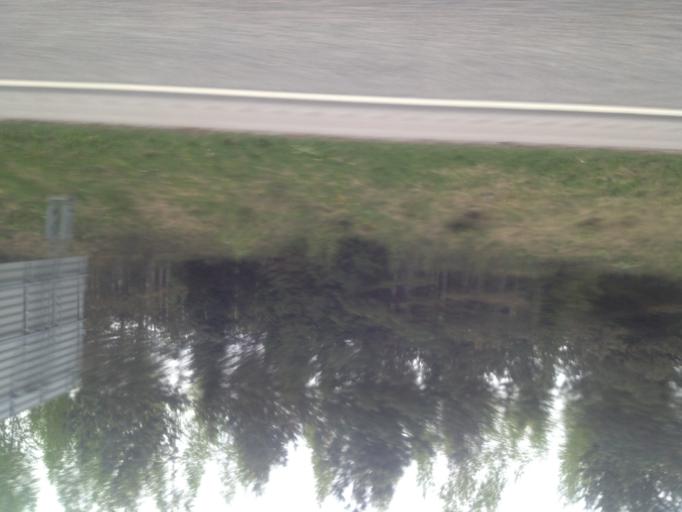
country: FI
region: Uusimaa
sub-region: Helsinki
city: Nurmijaervi
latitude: 60.4414
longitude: 24.8377
